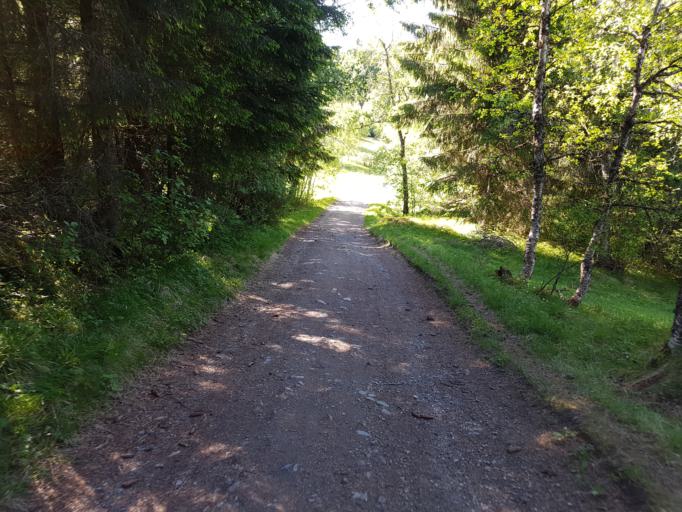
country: NO
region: Sor-Trondelag
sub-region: Trondheim
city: Trondheim
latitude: 63.4174
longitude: 10.3134
